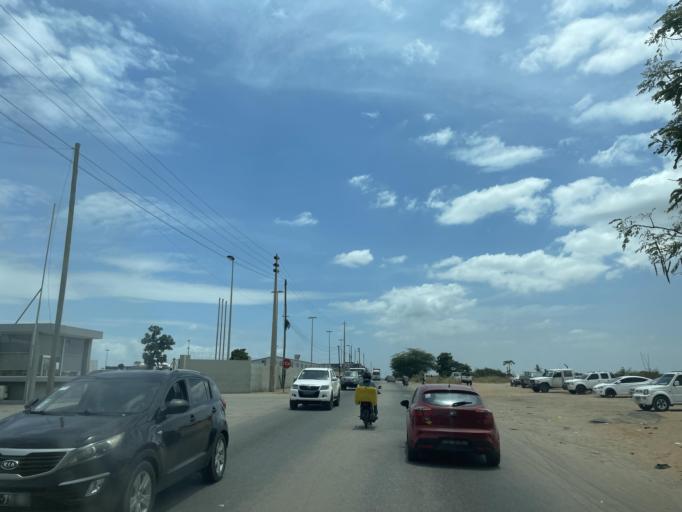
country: AO
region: Luanda
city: Luanda
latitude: -8.9367
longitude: 13.3902
